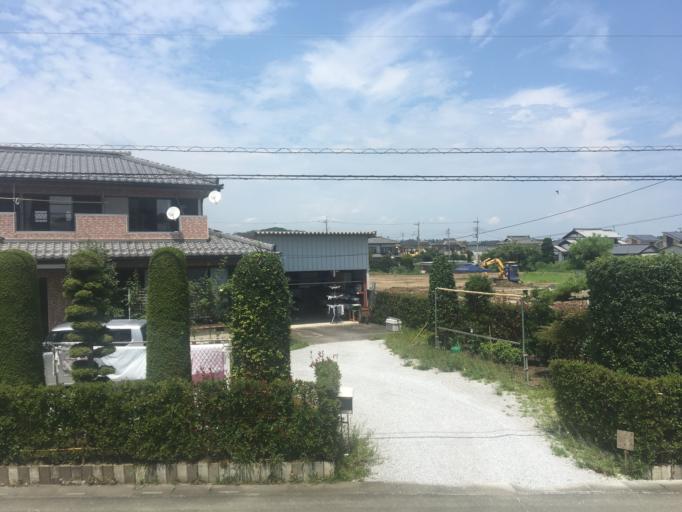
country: JP
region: Saitama
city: Kodamacho-kodamaminami
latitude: 36.1855
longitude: 139.1499
